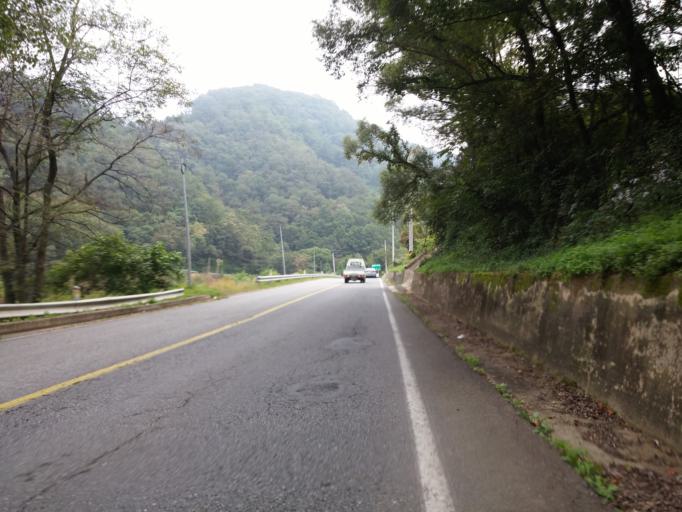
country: KR
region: Chungcheongbuk-do
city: Okcheon
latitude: 36.3924
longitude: 127.6758
